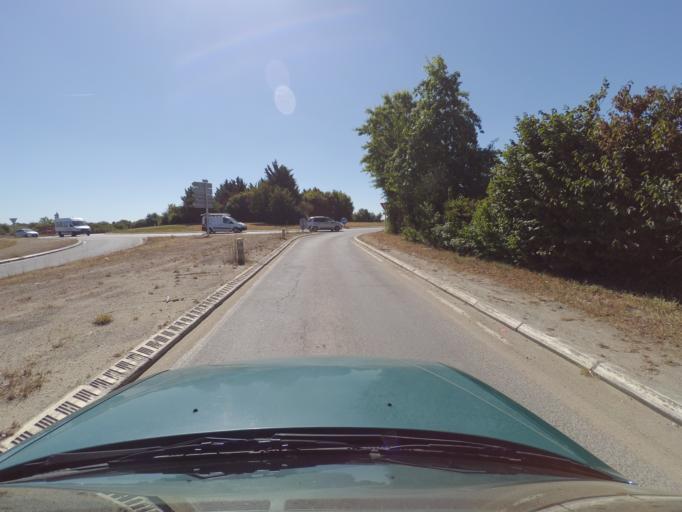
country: FR
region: Pays de la Loire
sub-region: Departement de la Loire-Atlantique
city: Les Sorinieres
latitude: 47.1122
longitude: -1.5397
